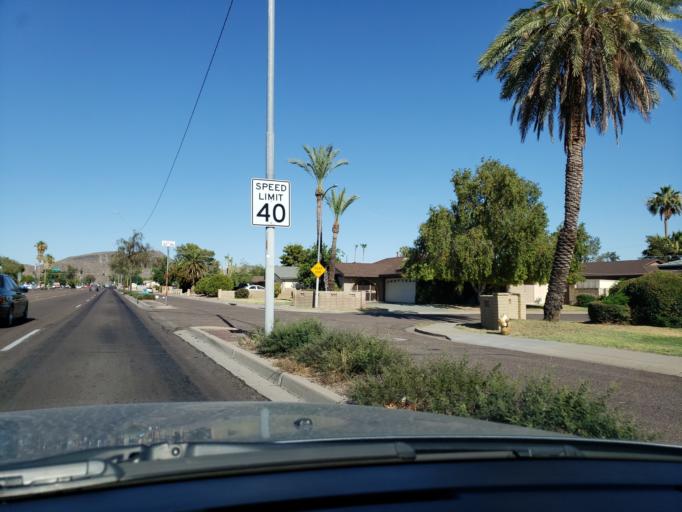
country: US
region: Arizona
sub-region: Maricopa County
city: Glendale
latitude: 33.5963
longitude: -112.1279
